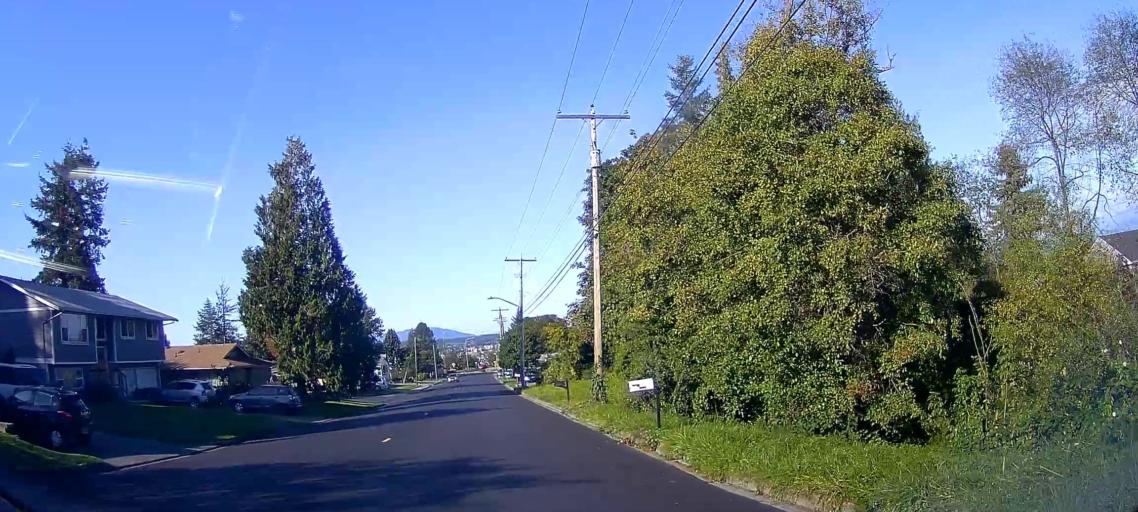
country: US
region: Washington
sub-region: Skagit County
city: Anacortes
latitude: 48.4911
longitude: -122.6128
